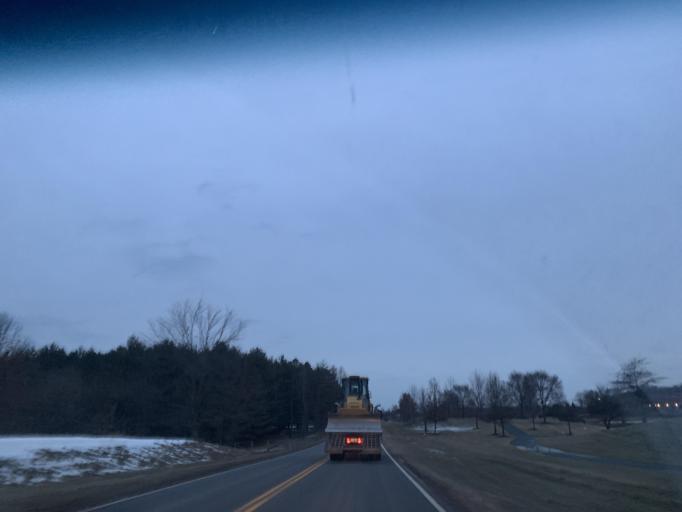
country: US
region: Ohio
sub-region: Union County
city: New California
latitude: 40.1434
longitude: -83.1817
